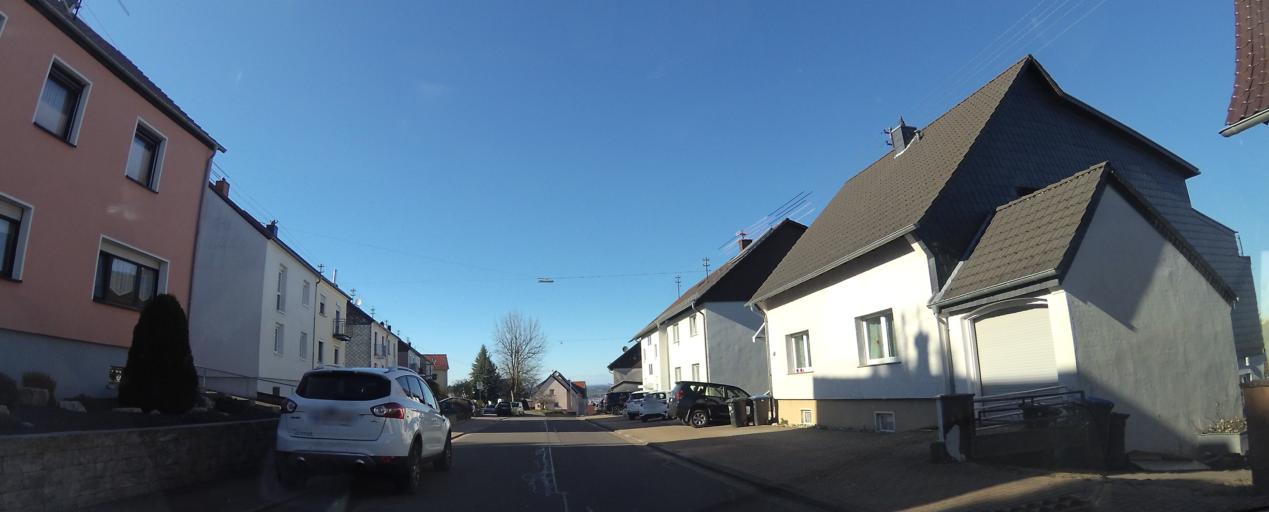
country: DE
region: Saarland
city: Riegelsberg
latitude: 49.3016
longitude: 6.9302
